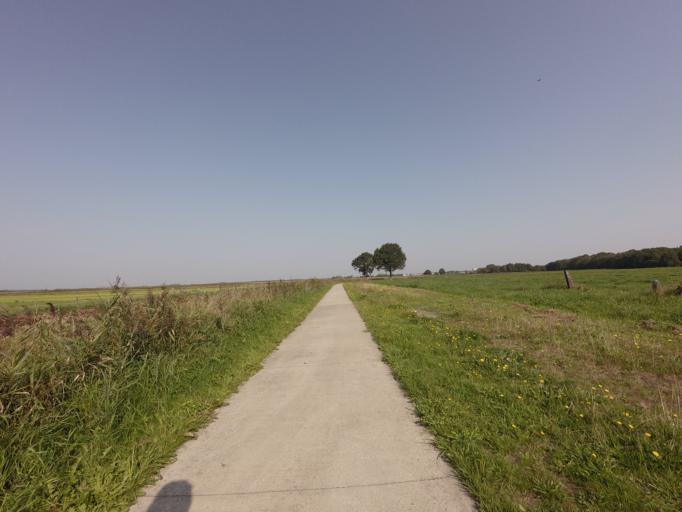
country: NL
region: Groningen
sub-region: Gemeente Groningen
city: Groningen
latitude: 53.1625
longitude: 6.5408
